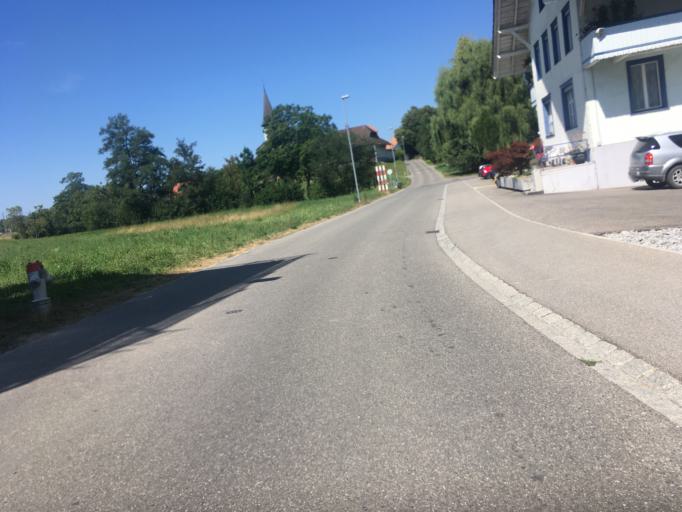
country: CH
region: Bern
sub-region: Bern-Mittelland District
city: Fraubrunnen
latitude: 47.0842
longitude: 7.5195
